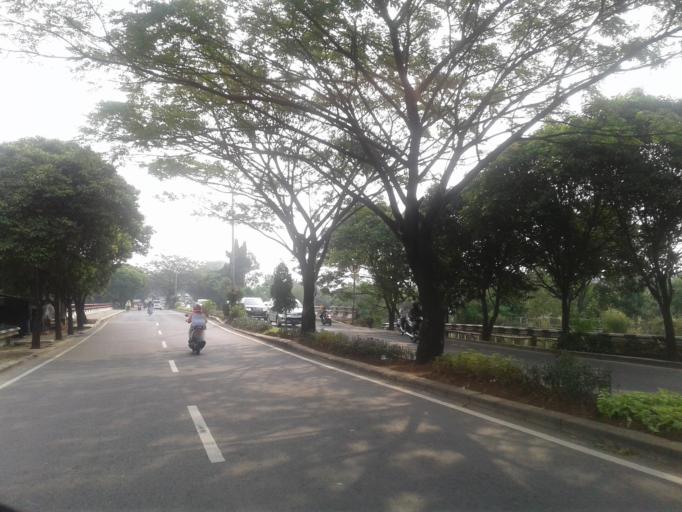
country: ID
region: West Java
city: Depok
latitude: -6.3811
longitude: 106.8584
